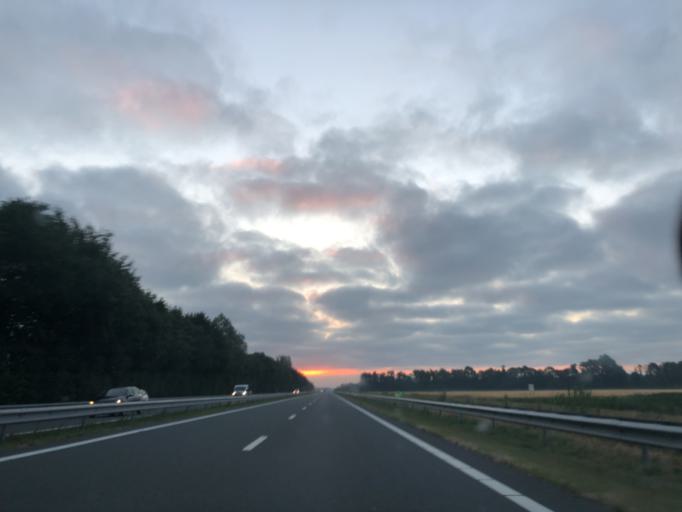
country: NL
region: Drenthe
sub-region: Gemeente Aa en Hunze
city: Anloo
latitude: 53.0260
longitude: 6.7866
